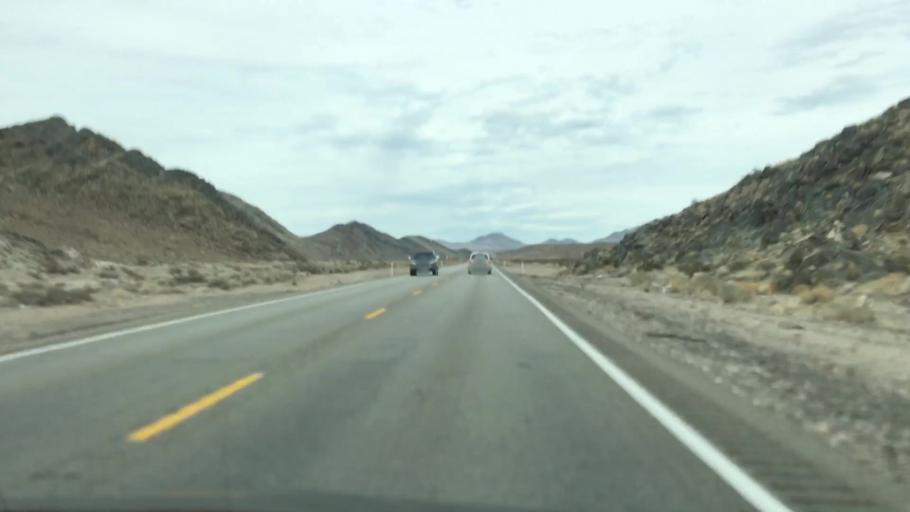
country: US
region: Nevada
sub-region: Nye County
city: Pahrump
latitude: 36.5663
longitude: -116.0833
